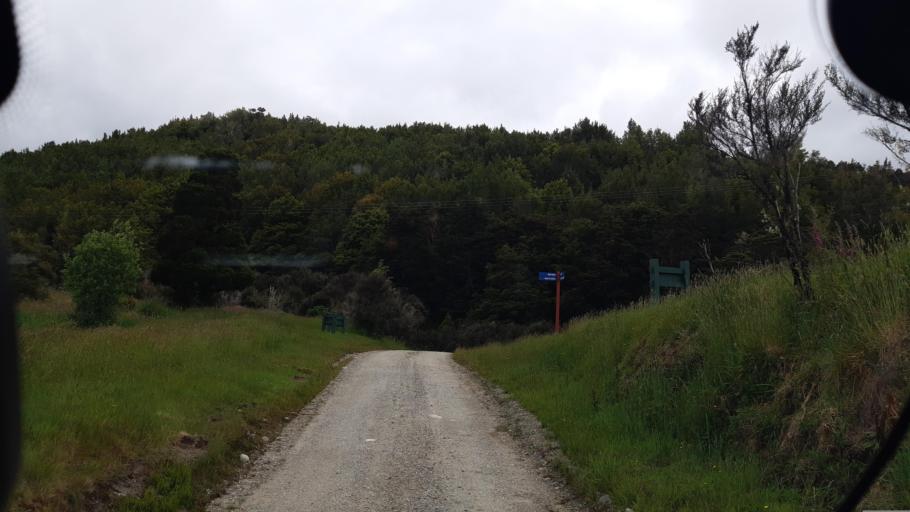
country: NZ
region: West Coast
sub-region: Buller District
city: Westport
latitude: -42.2899
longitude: 171.8194
